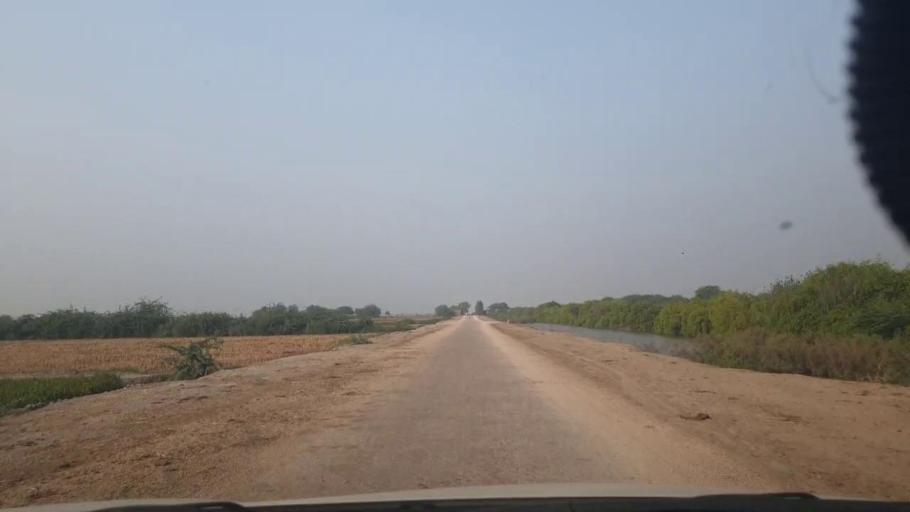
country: PK
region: Sindh
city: Bulri
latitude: 24.8339
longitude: 68.4030
